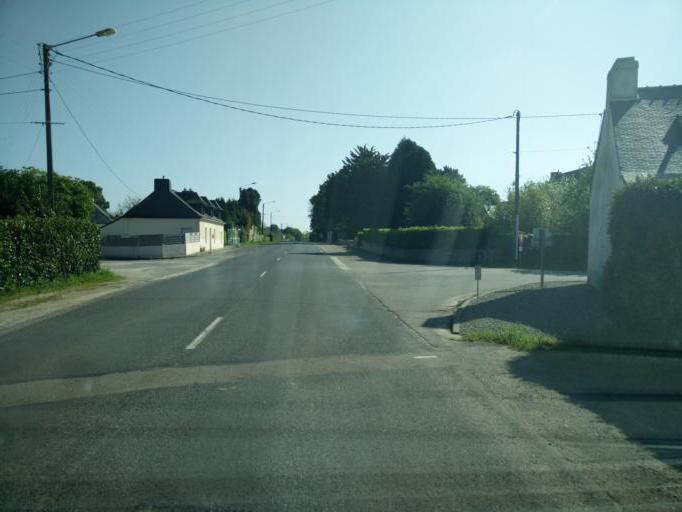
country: FR
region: Brittany
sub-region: Departement du Morbihan
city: Branderion
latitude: 47.8246
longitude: -3.2006
